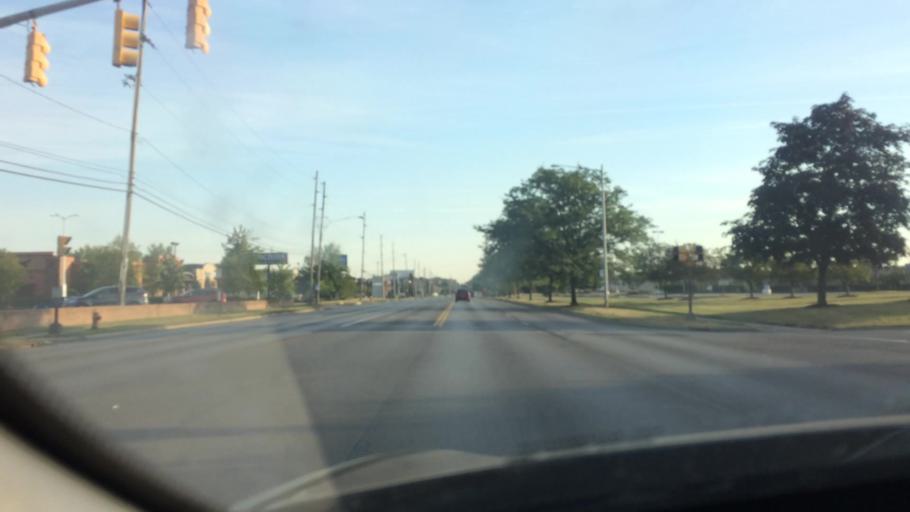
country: US
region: Ohio
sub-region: Lucas County
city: Ottawa Hills
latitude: 41.6934
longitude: -83.6447
